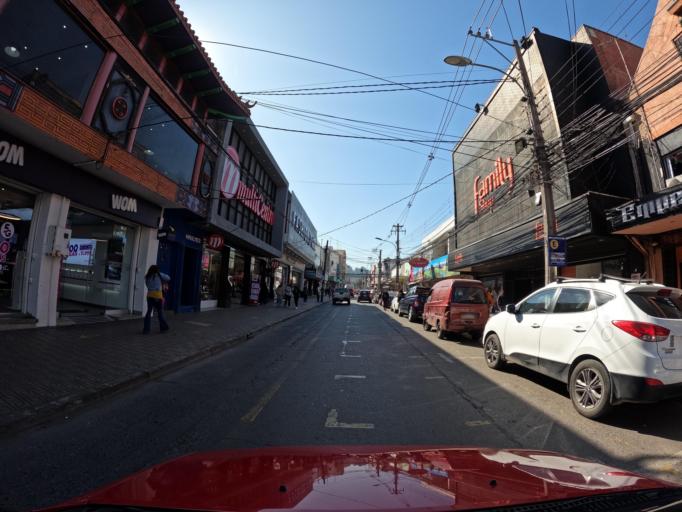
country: CL
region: Maule
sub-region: Provincia de Curico
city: Curico
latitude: -34.9839
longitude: -71.2425
